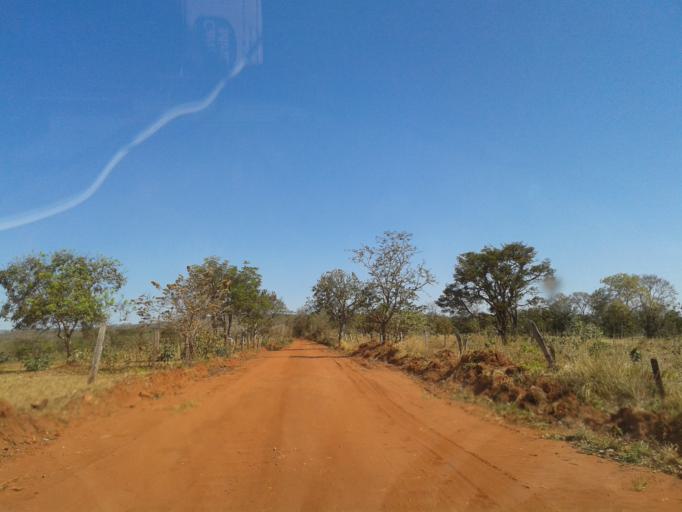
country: BR
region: Minas Gerais
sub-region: Ituiutaba
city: Ituiutaba
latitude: -19.0789
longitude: -49.3371
